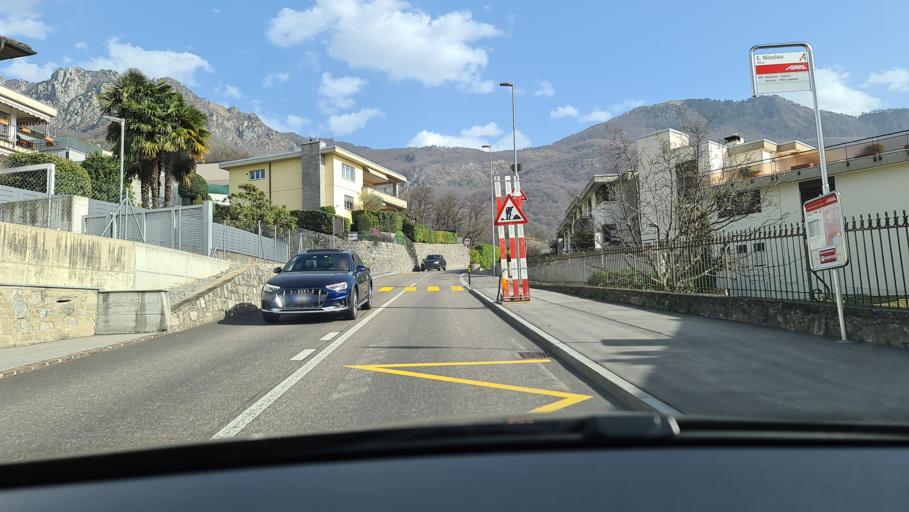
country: CH
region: Ticino
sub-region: Lugano District
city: Cadro
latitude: 46.0538
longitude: 8.9851
